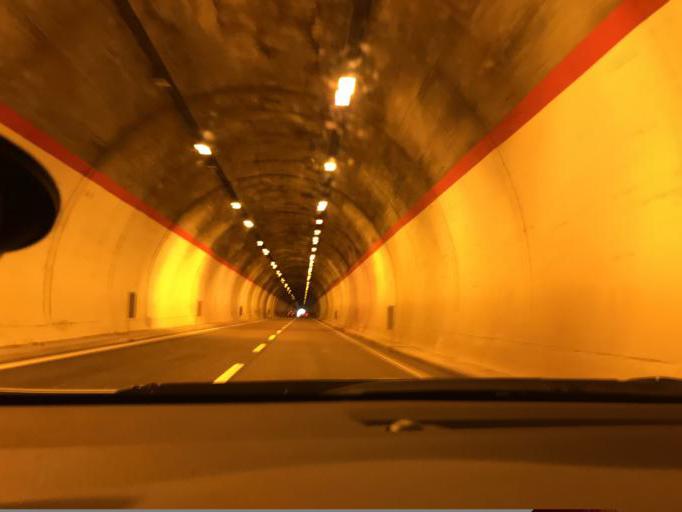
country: IT
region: Umbria
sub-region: Provincia di Perugia
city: Via Lippia
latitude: 43.1090
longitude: 12.4925
